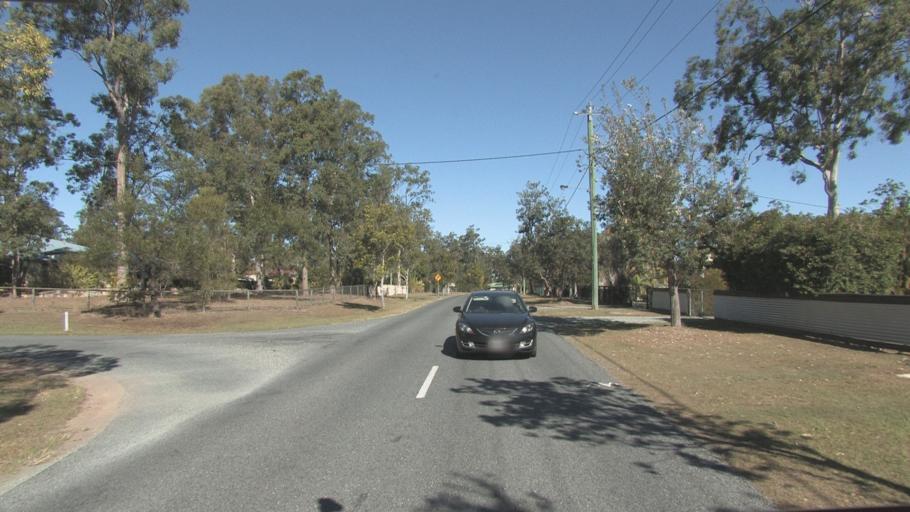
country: AU
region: Queensland
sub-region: Logan
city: North Maclean
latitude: -27.7394
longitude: 152.9594
